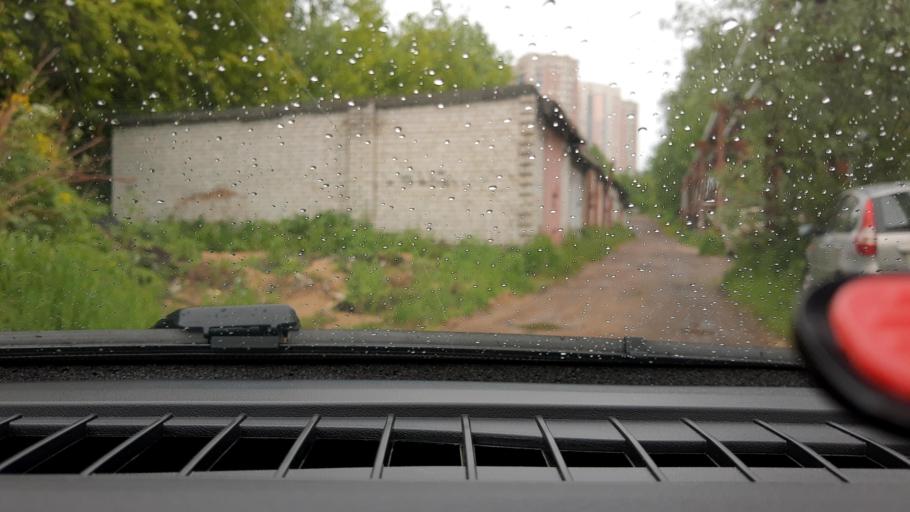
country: RU
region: Nizjnij Novgorod
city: Bor
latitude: 56.3127
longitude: 44.0609
